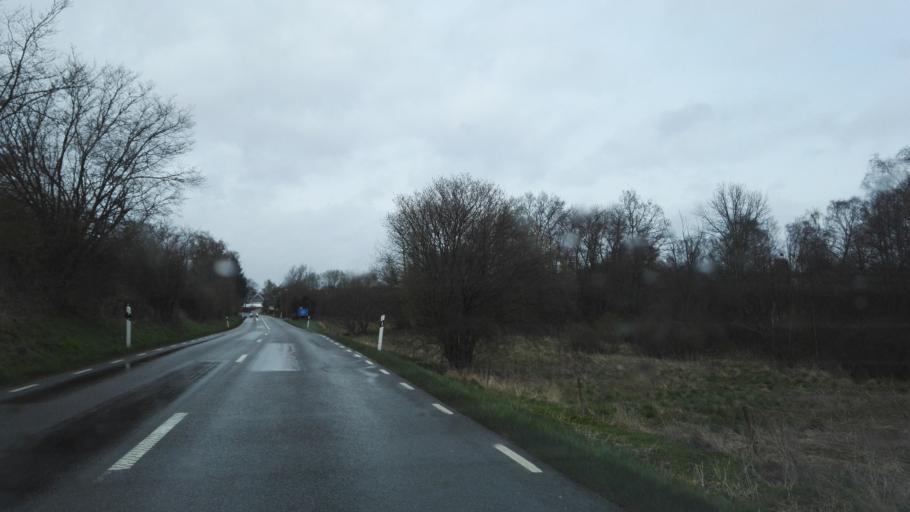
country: SE
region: Skane
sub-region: Simrishamns Kommun
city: Kivik
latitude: 55.6591
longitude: 14.2211
